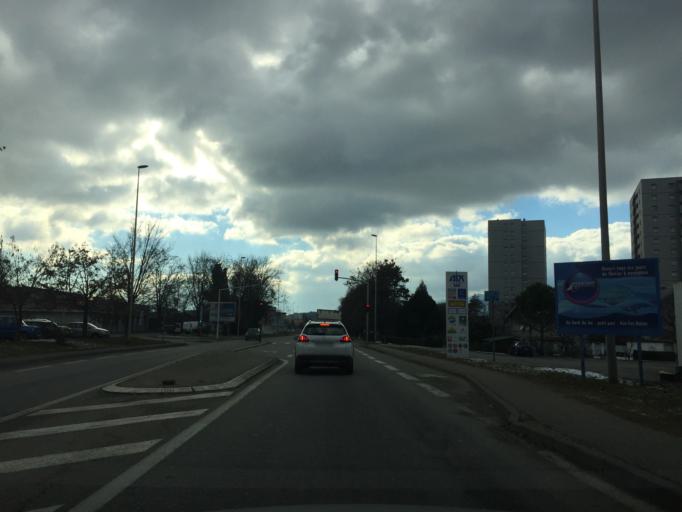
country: FR
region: Rhone-Alpes
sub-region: Departement de la Savoie
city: Brison-Saint-Innocent
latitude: 45.7084
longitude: 5.9117
